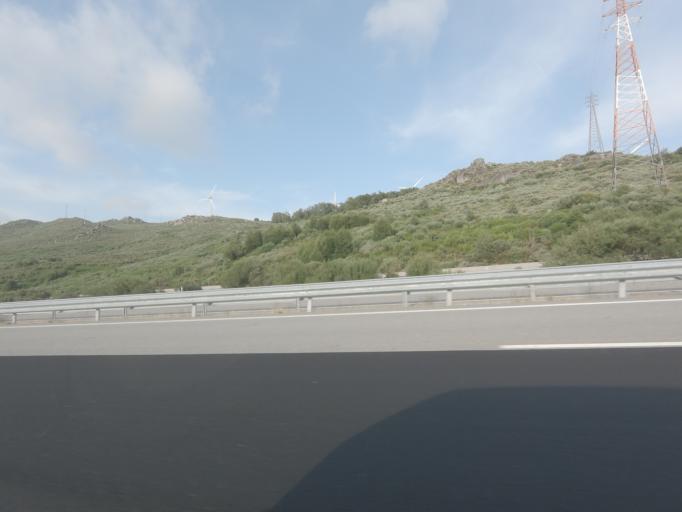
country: PT
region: Vila Real
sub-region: Vila Pouca de Aguiar
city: Vila Pouca de Aguiar
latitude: 41.4594
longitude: -7.6436
